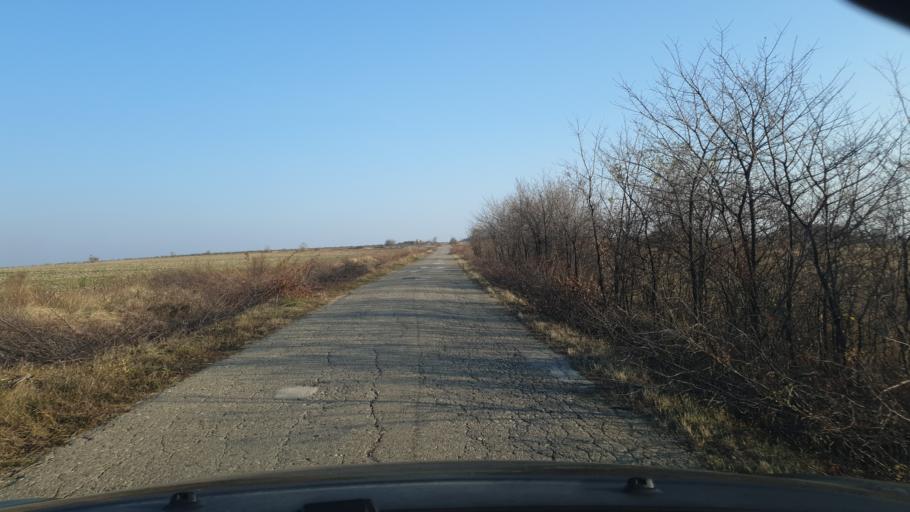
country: RS
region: Central Serbia
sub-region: Borski Okrug
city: Negotin
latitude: 44.1222
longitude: 22.3512
